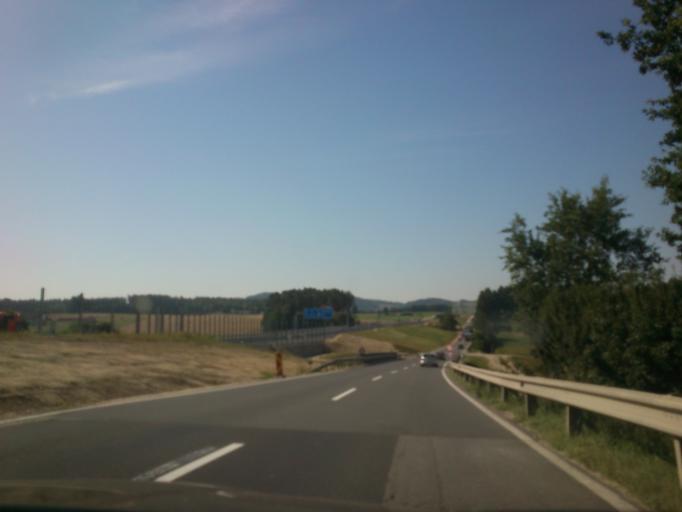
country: AT
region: Upper Austria
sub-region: Politischer Bezirk Freistadt
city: Freistadt
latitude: 48.4638
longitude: 14.5024
